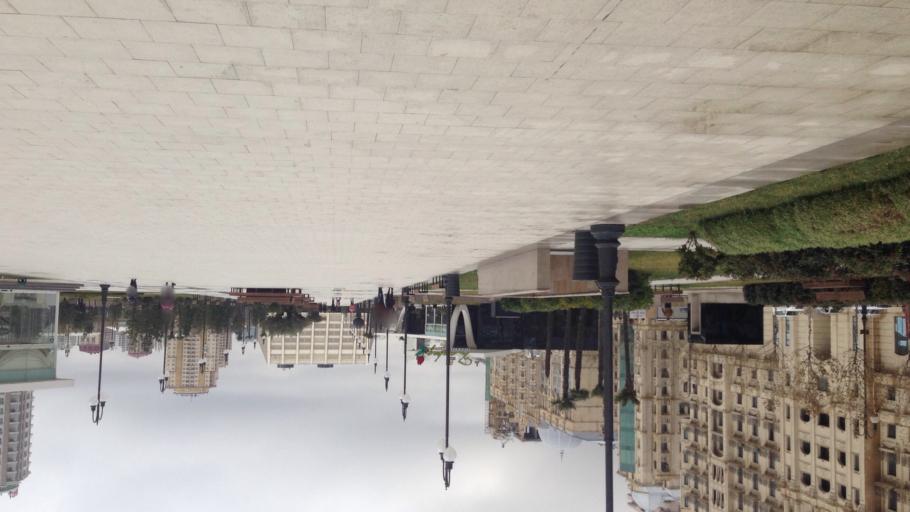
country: AZ
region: Baki
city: Badamdar
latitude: 40.3770
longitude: 49.8367
